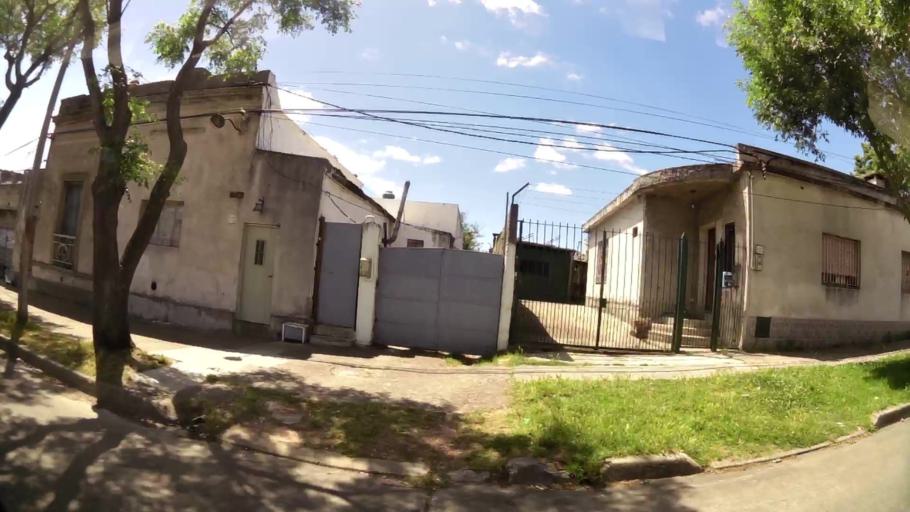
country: UY
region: Montevideo
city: Montevideo
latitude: -34.8594
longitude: -56.1307
